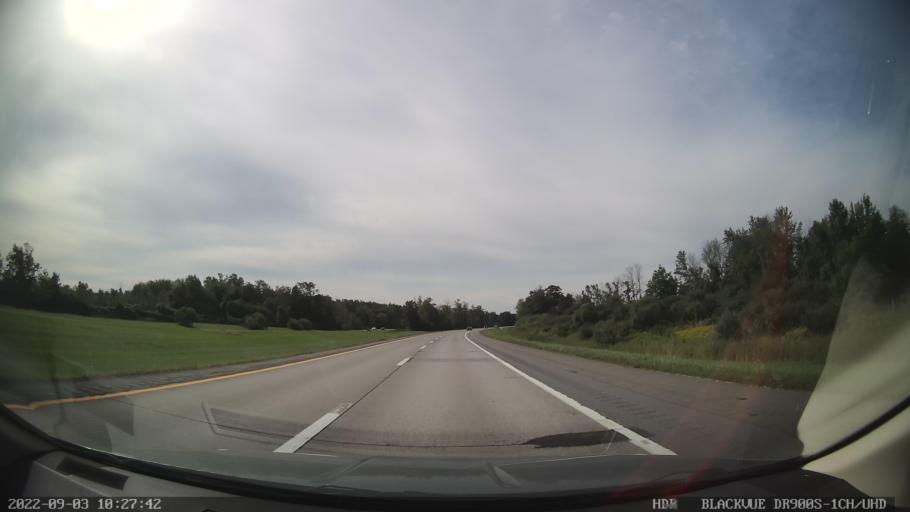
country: US
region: New York
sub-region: Livingston County
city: Livonia
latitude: 42.8122
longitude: -77.7381
